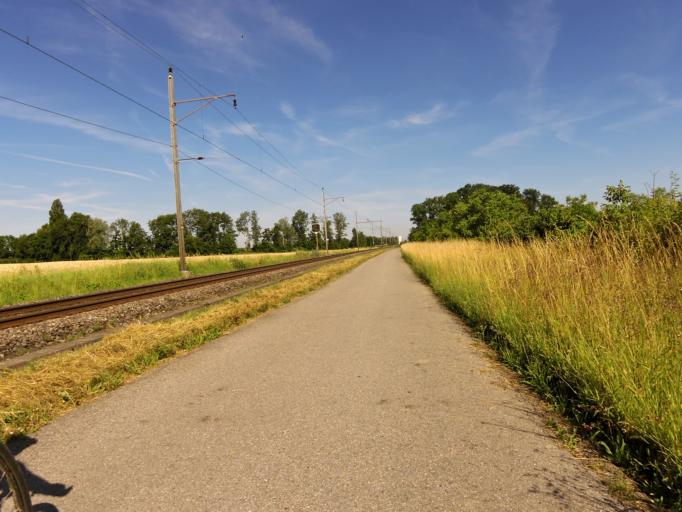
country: CH
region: Thurgau
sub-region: Kreuzlingen District
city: Guttingen
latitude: 47.6017
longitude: 9.3054
